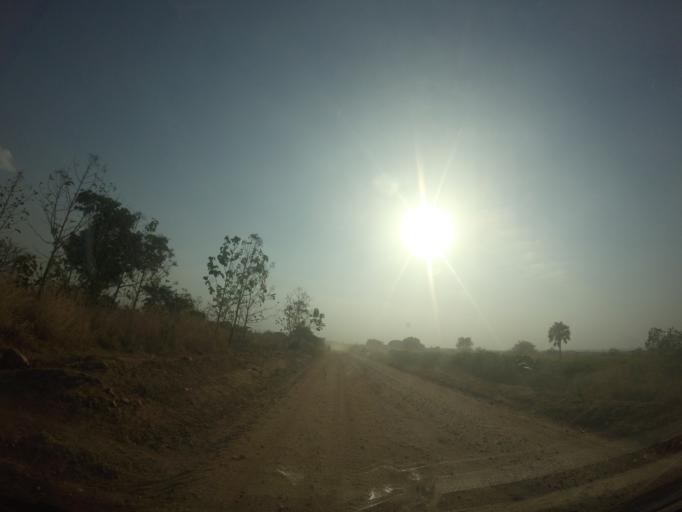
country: UG
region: Northern Region
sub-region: Arua District
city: Arua
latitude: 3.1013
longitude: 31.1045
